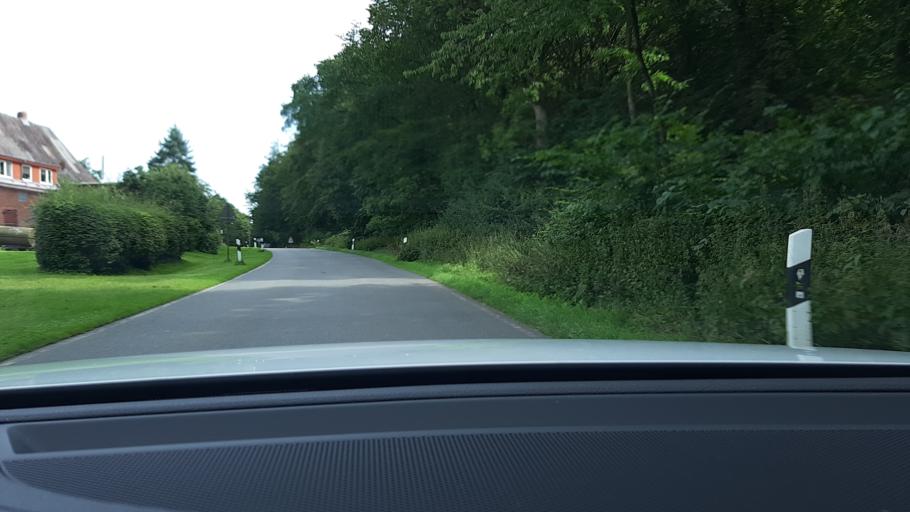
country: DE
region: Schleswig-Holstein
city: Rehhorst
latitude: 53.8567
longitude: 10.4671
